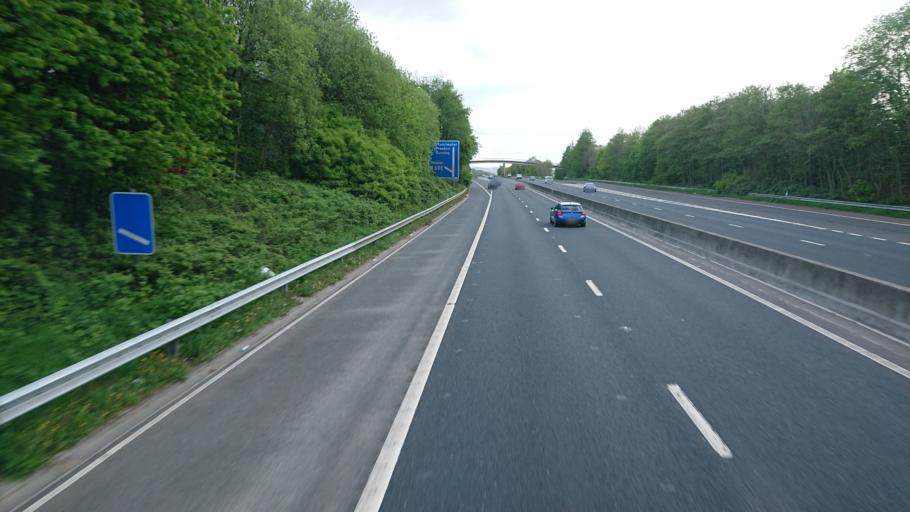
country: GB
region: England
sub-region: Lancashire
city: Barrowford
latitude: 53.8474
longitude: -2.2144
